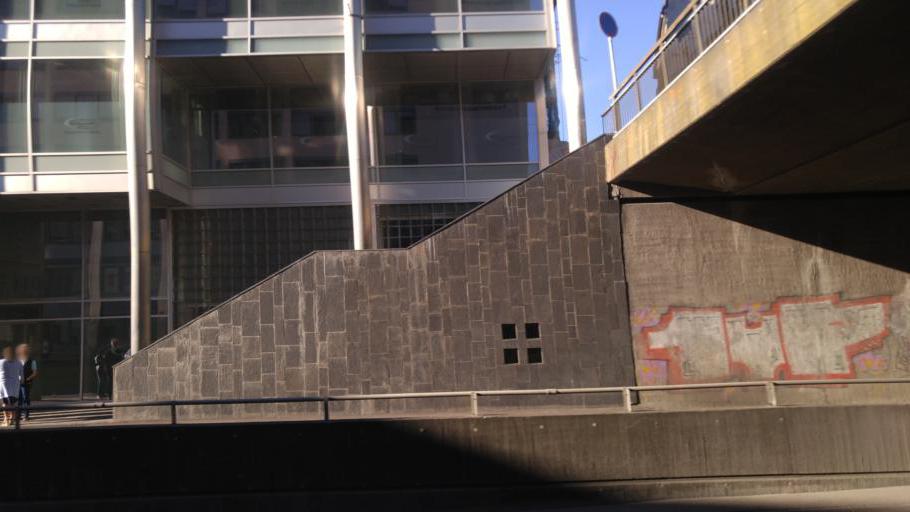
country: NO
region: Oslo
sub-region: Oslo
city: Oslo
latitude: 59.9161
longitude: 10.7492
